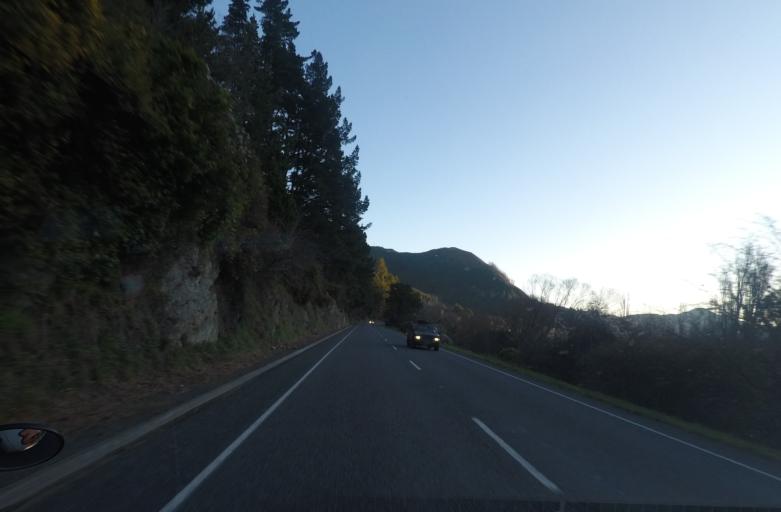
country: NZ
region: Marlborough
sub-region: Marlborough District
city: Picton
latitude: -41.2859
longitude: 173.7091
